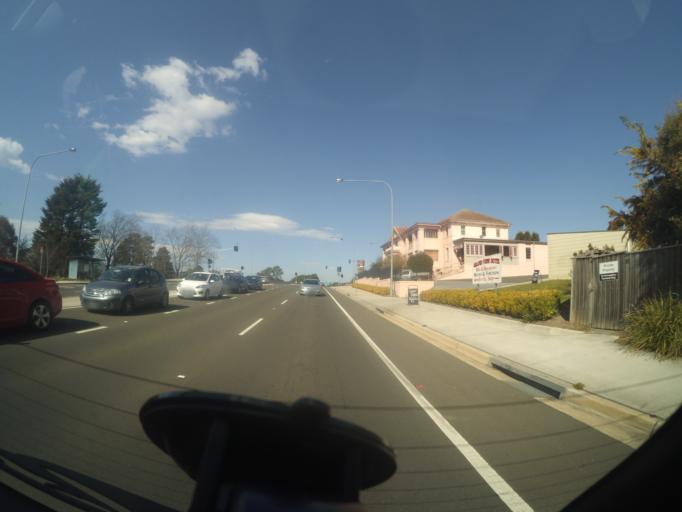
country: AU
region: New South Wales
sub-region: Blue Mountains Municipality
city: Leura
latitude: -33.7106
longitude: 150.3757
